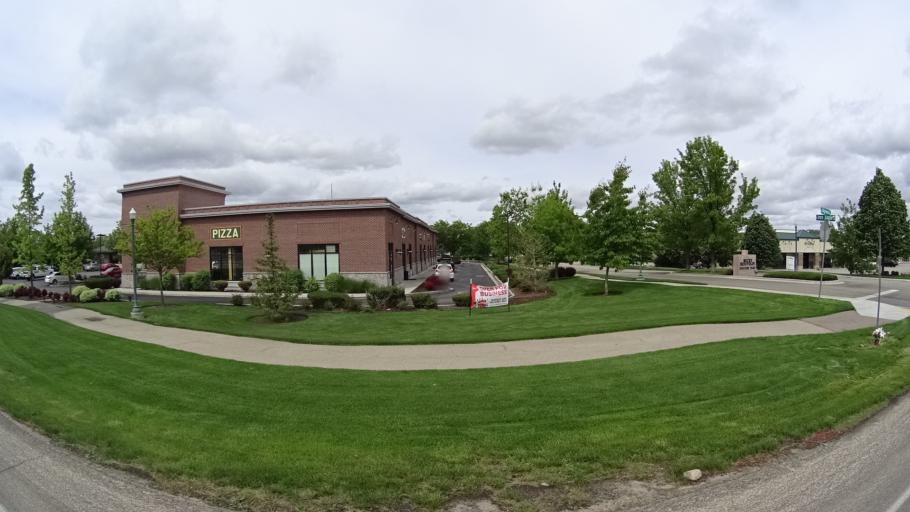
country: US
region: Idaho
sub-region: Ada County
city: Eagle
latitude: 43.6893
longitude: -116.3339
